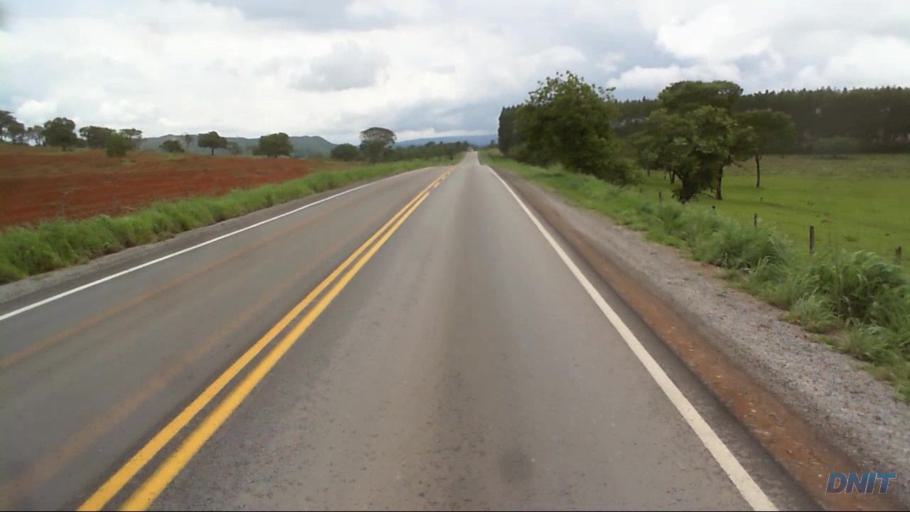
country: BR
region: Goias
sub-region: Padre Bernardo
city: Padre Bernardo
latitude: -15.5036
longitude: -48.2054
